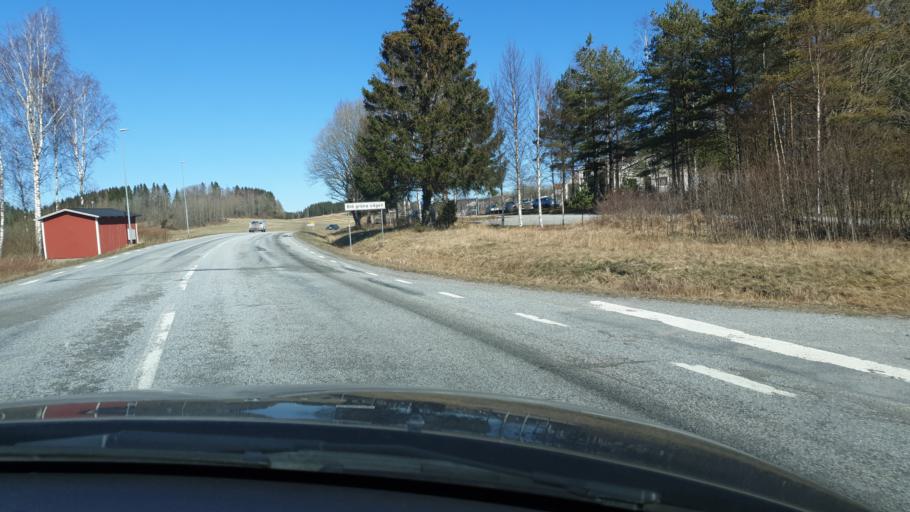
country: SE
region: Vaestra Goetaland
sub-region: Tanums Kommun
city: Tanumshede
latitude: 58.7693
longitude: 11.5566
